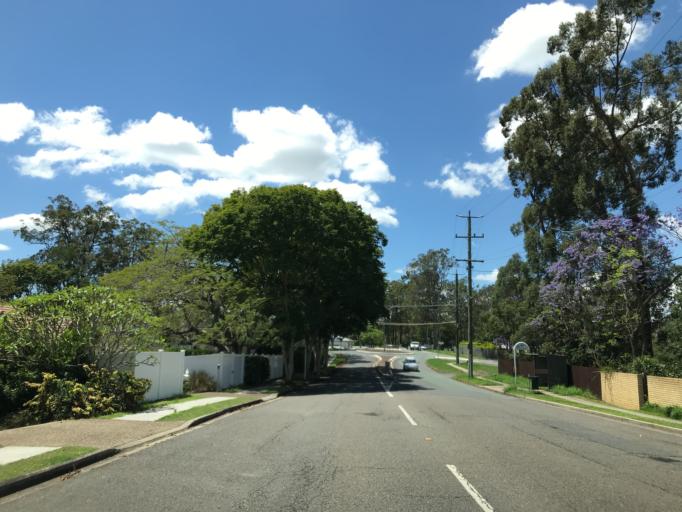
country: AU
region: Queensland
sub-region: Brisbane
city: Kenmore Hills
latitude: -27.5243
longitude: 152.9494
